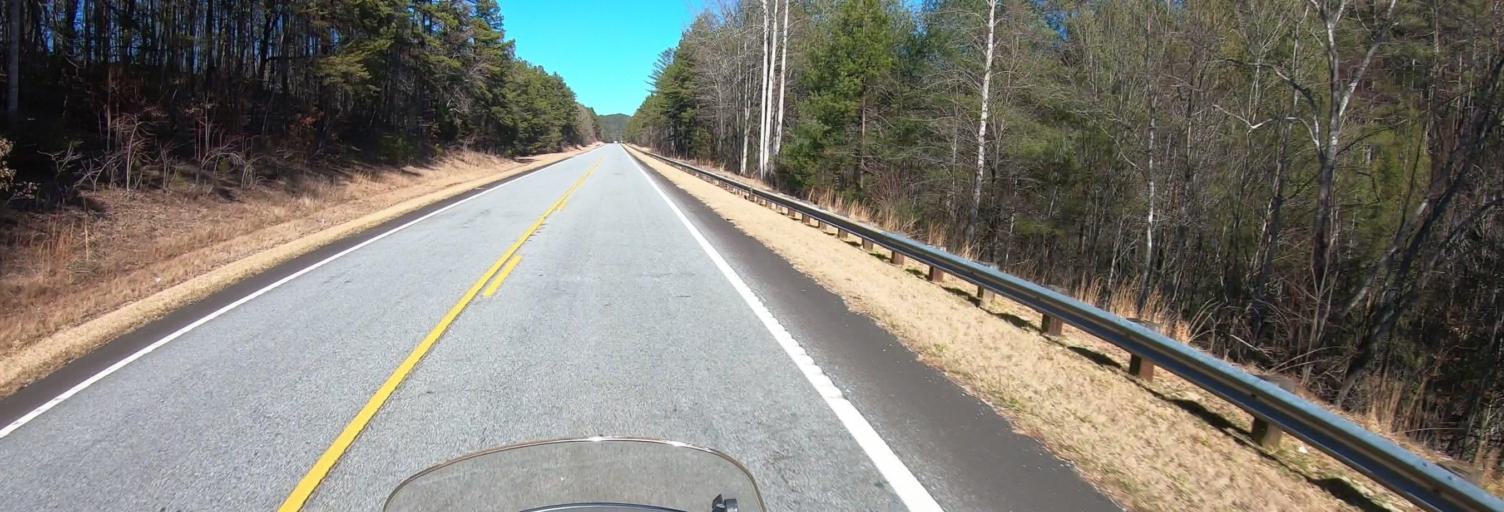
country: US
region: South Carolina
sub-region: Pickens County
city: Pickens
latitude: 34.9505
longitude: -82.8522
